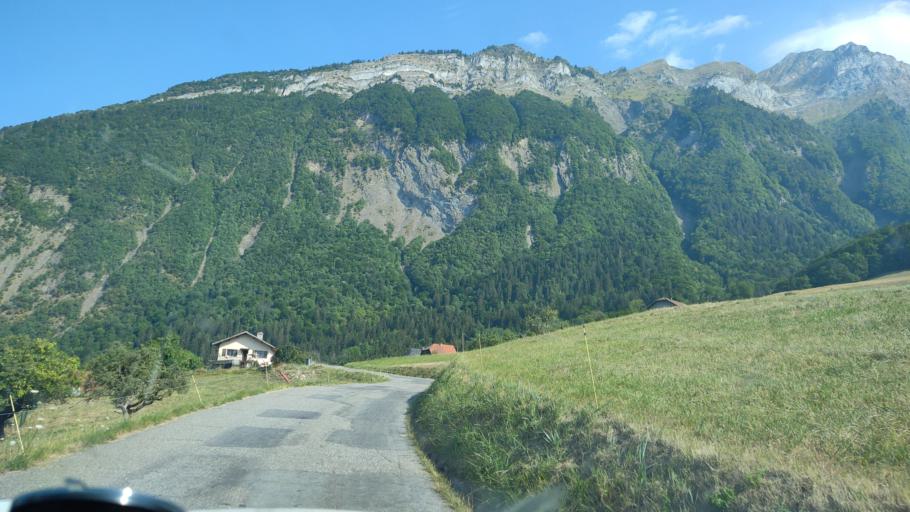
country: FR
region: Rhone-Alpes
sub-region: Departement de la Savoie
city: Ugine
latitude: 45.7678
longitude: 6.4026
